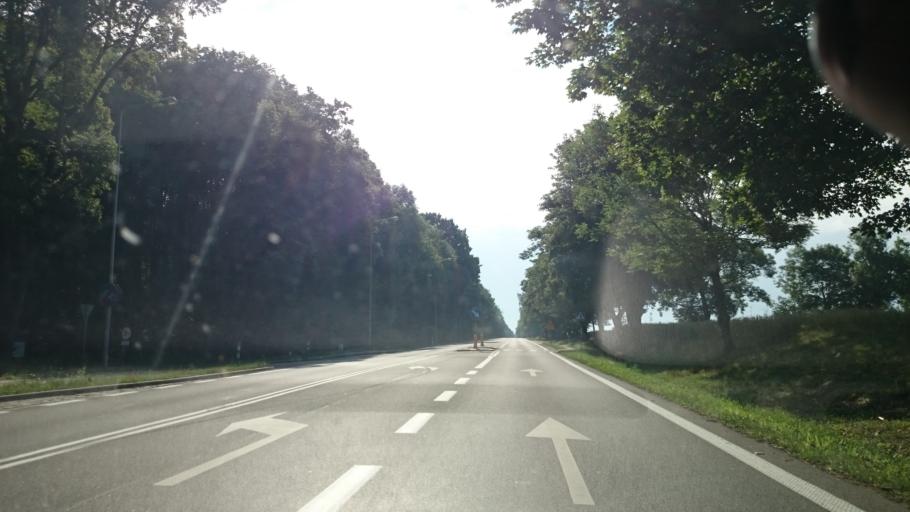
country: PL
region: Opole Voivodeship
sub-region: Powiat strzelecki
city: Strzelce Opolskie
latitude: 50.5018
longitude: 18.3398
